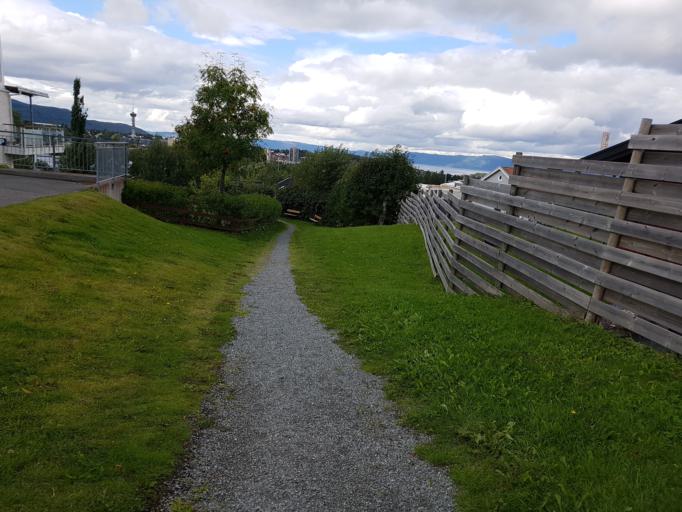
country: NO
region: Sor-Trondelag
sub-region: Trondheim
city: Trondheim
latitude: 63.4150
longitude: 10.4667
